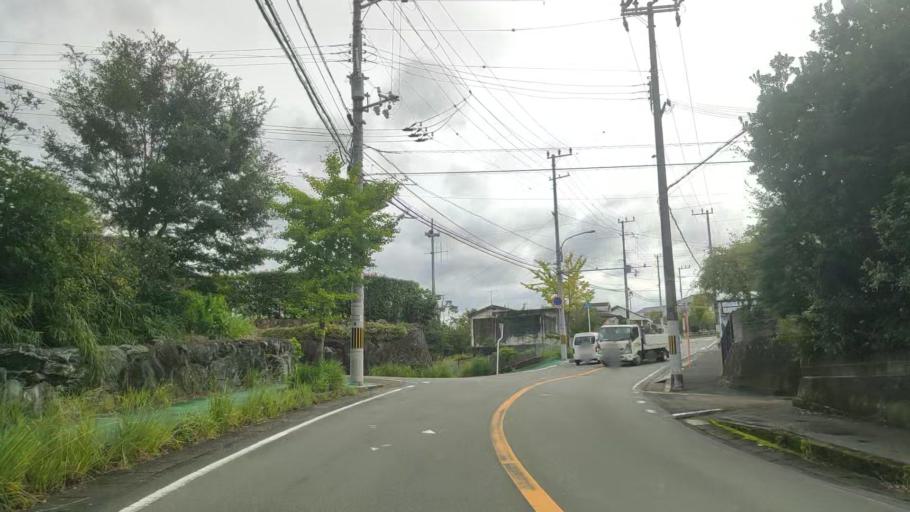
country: JP
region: Wakayama
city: Tanabe
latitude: 33.6768
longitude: 135.3749
